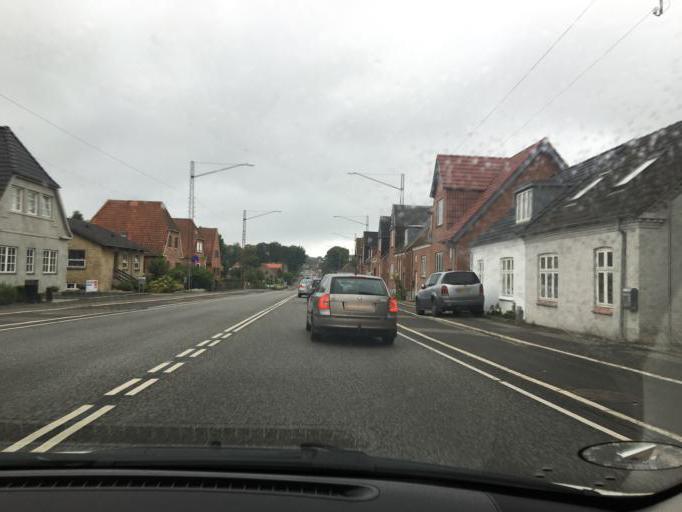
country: DK
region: South Denmark
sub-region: Middelfart Kommune
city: Middelfart
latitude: 55.5003
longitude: 9.7368
